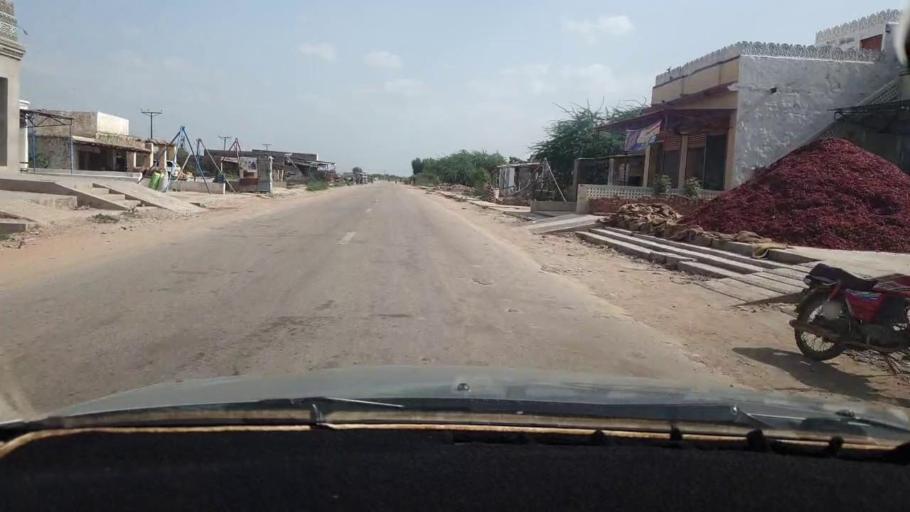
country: PK
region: Sindh
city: Naukot
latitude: 24.9022
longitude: 69.3307
